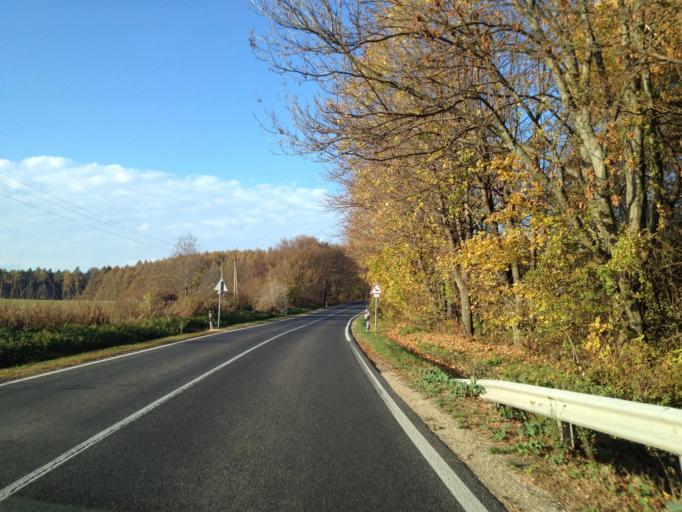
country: HU
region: Veszprem
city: Zirc
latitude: 47.3159
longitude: 17.8774
